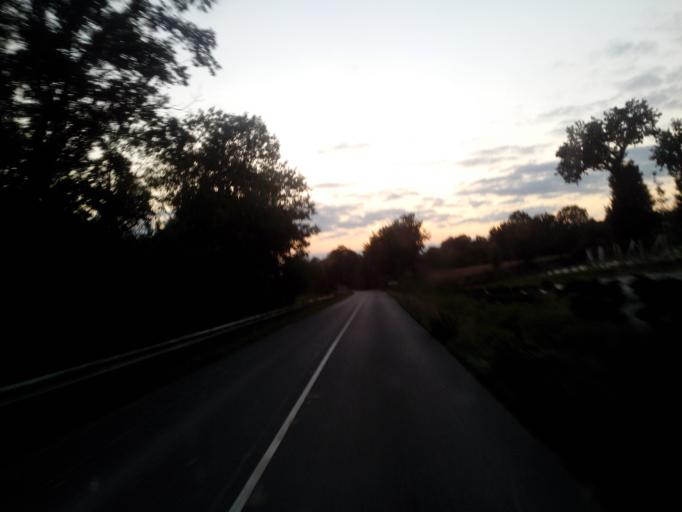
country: FR
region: Brittany
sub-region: Departement d'Ille-et-Vilaine
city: Montfort-sur-Meu
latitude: 48.1380
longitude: -1.9727
